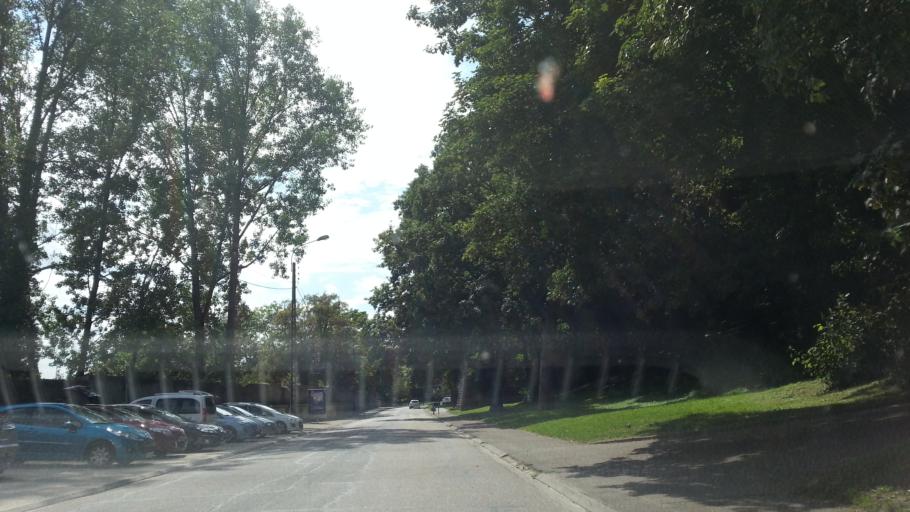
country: FR
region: Lorraine
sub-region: Departement de la Meuse
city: Verdun
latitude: 49.1574
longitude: 5.3762
